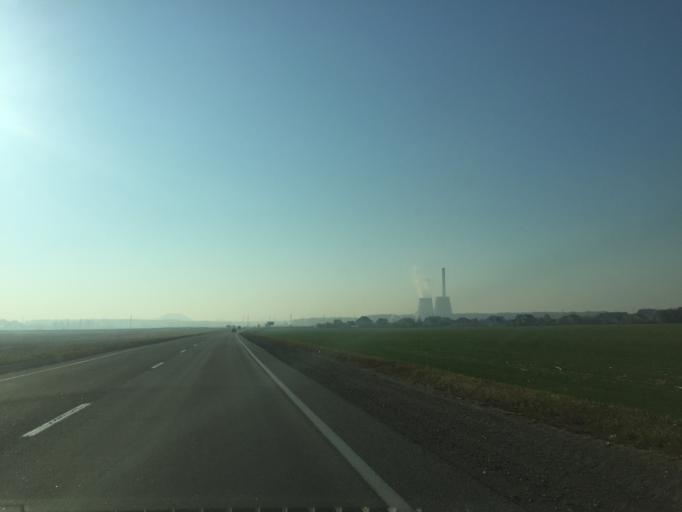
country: BY
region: Gomel
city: Kastsyukowka
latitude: 52.4687
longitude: 30.8238
